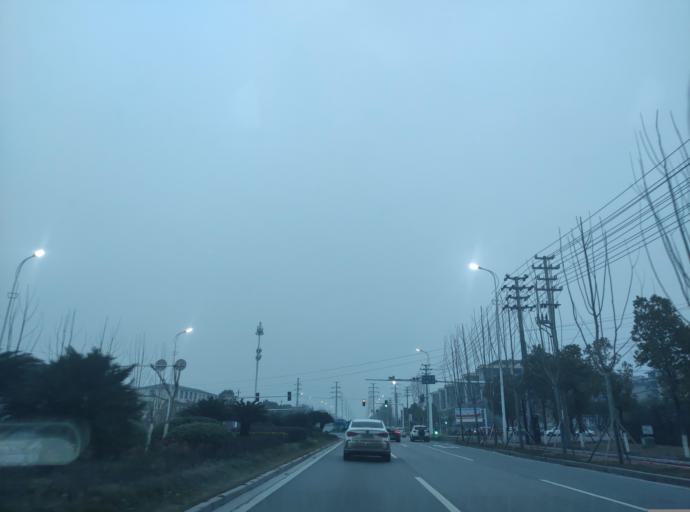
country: CN
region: Jiangxi Sheng
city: Pingxiang
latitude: 27.6688
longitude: 113.8729
